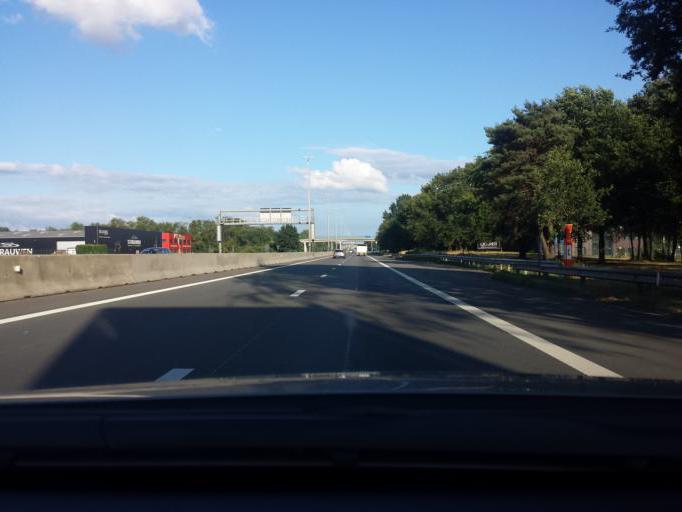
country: BE
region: Flanders
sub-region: Provincie Antwerpen
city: Vorselaar
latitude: 51.1655
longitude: 4.7877
